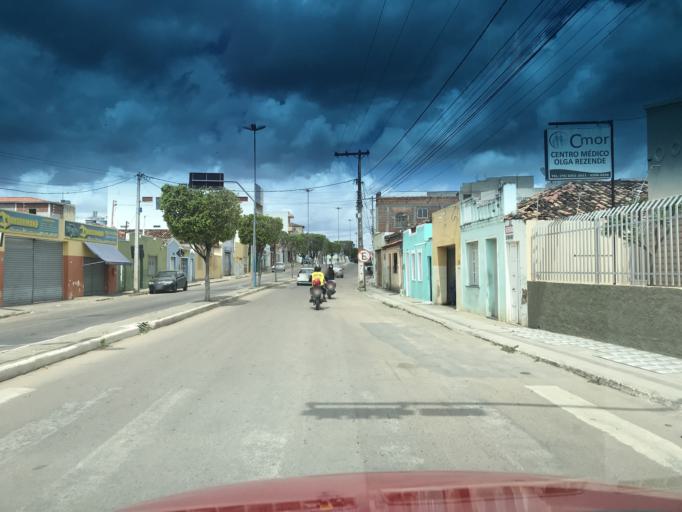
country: BR
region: Bahia
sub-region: Itaberaba
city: Itaberaba
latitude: -12.5282
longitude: -40.3073
